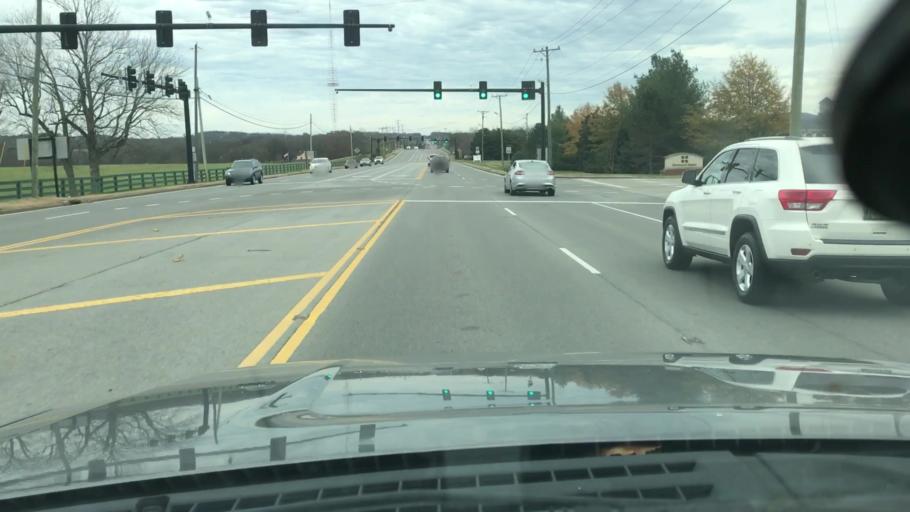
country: US
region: Tennessee
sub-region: Williamson County
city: Brentwood Estates
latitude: 35.9986
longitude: -86.8060
